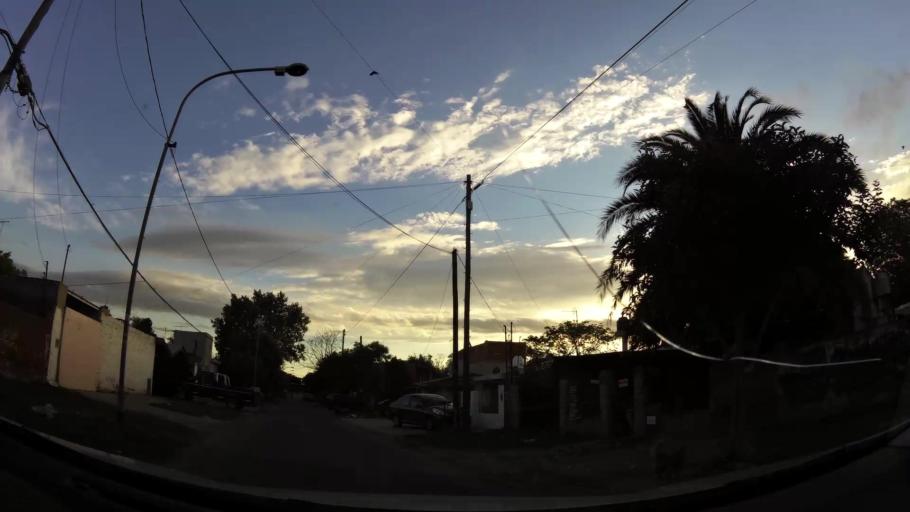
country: AR
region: Buenos Aires
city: Santa Catalina - Dique Lujan
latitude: -34.4476
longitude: -58.6654
